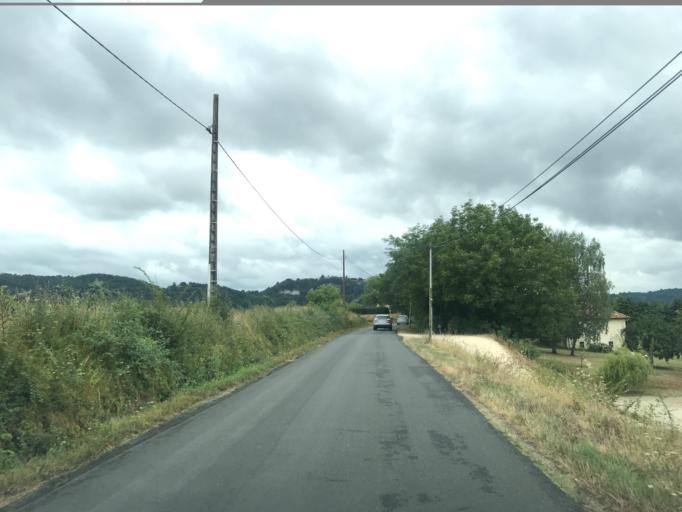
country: FR
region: Aquitaine
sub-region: Departement de la Dordogne
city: Domme
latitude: 44.8191
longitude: 1.2280
